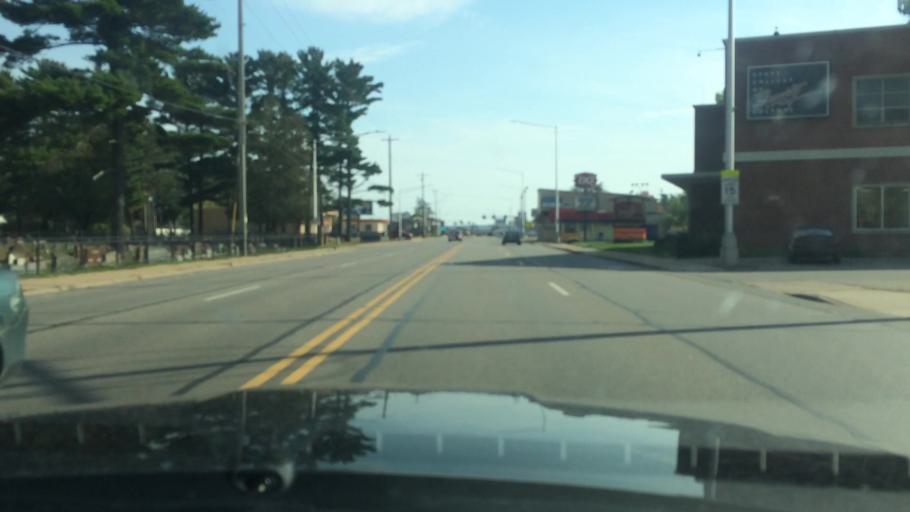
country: US
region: Wisconsin
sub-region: Marathon County
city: Wausau
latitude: 44.9374
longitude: -89.6178
